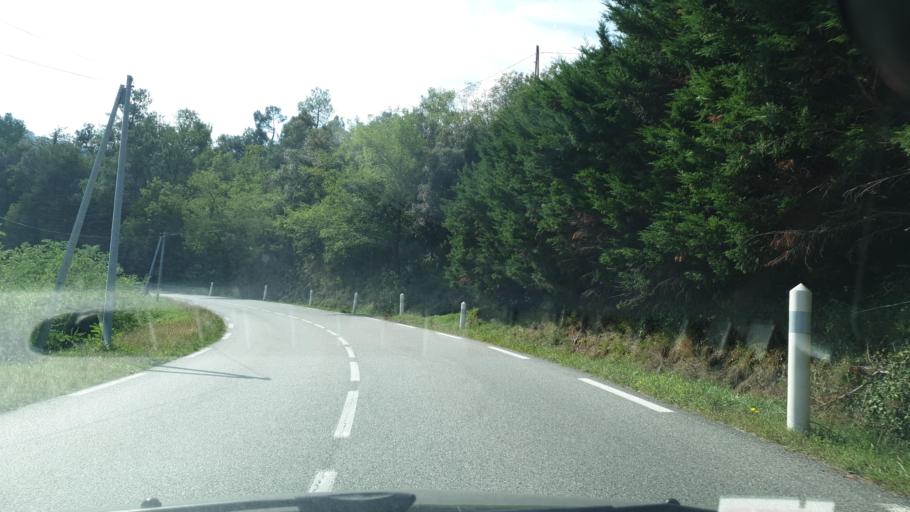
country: FR
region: Rhone-Alpes
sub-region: Departement de l'Ardeche
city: Saint-Sauveur-de-Montagut
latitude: 44.8172
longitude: 4.6377
